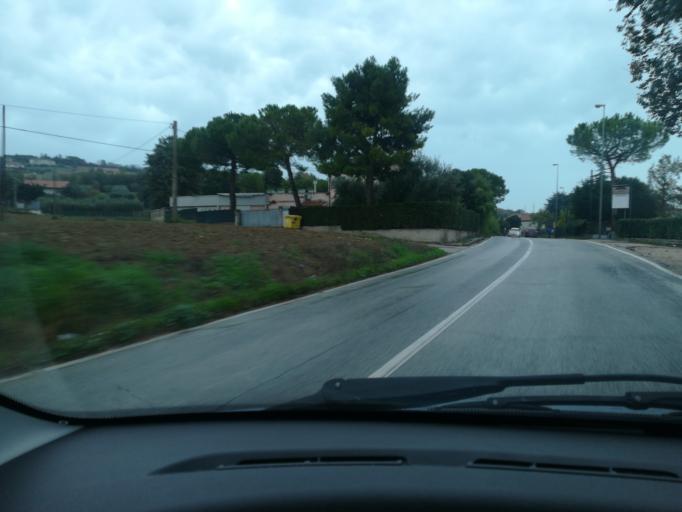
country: IT
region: The Marches
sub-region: Provincia di Macerata
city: Santa Maria Apparente
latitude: 43.2954
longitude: 13.6823
